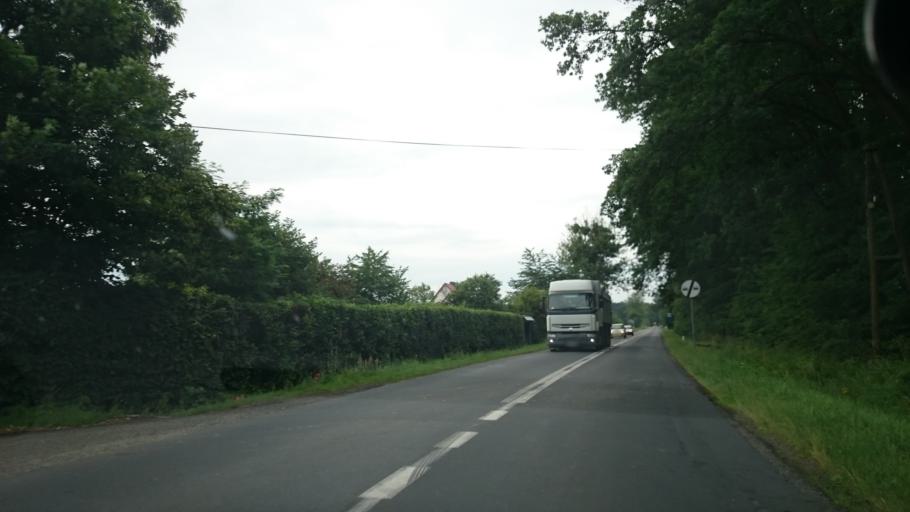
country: PL
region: Opole Voivodeship
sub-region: Powiat brzeski
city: Grodkow
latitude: 50.6554
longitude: 17.4360
